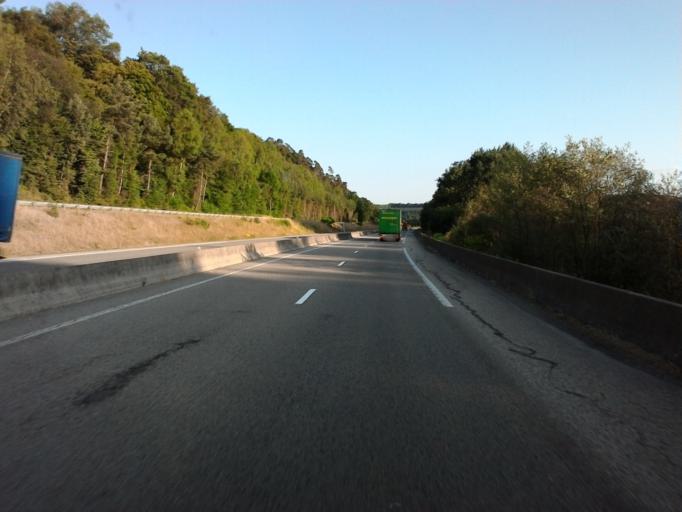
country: FR
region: Lorraine
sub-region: Departement des Vosges
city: Arches
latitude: 48.1375
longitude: 6.5144
